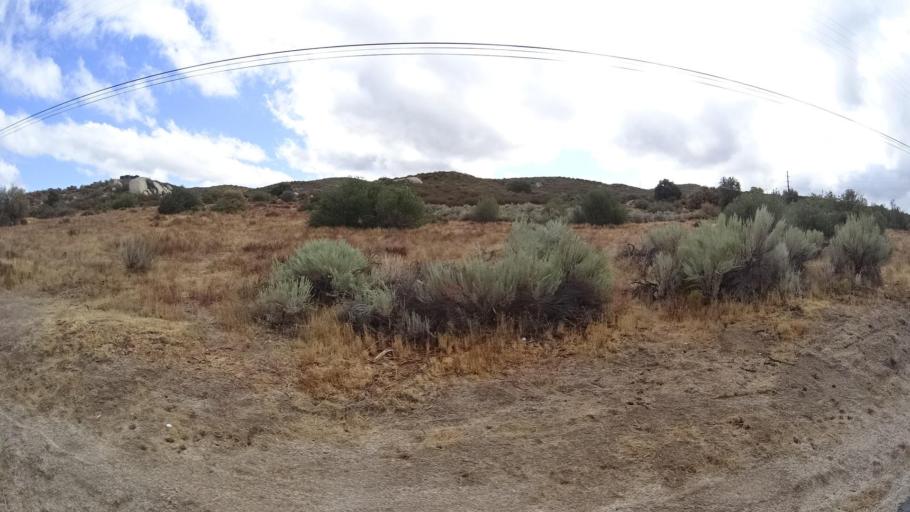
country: US
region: California
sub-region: San Diego County
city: Campo
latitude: 32.7187
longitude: -116.4292
